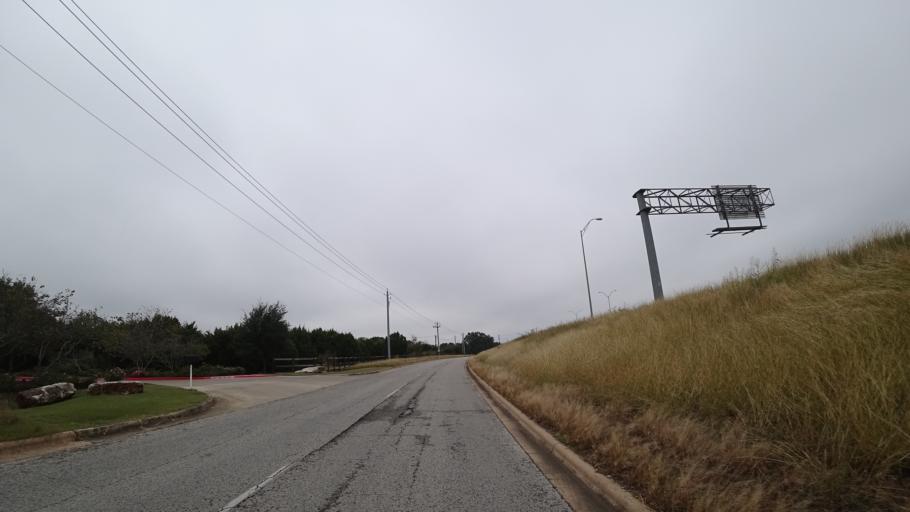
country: US
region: Texas
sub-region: Travis County
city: Shady Hollow
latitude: 30.2163
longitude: -97.8414
